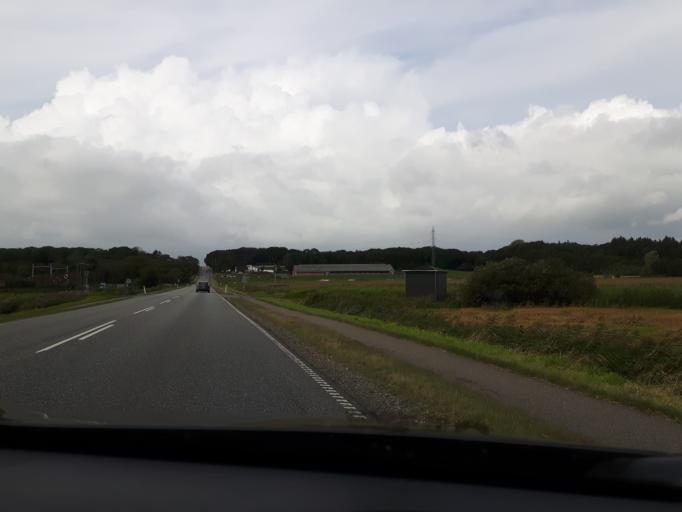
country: DK
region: North Denmark
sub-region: Jammerbugt Kommune
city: Brovst
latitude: 57.0963
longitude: 9.5060
